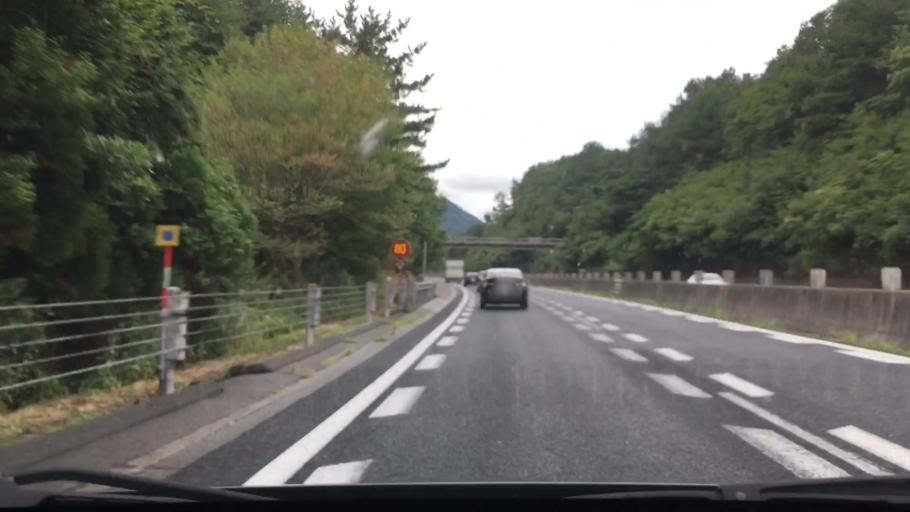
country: JP
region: Hiroshima
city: Hiroshima-shi
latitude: 34.5964
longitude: 132.4884
